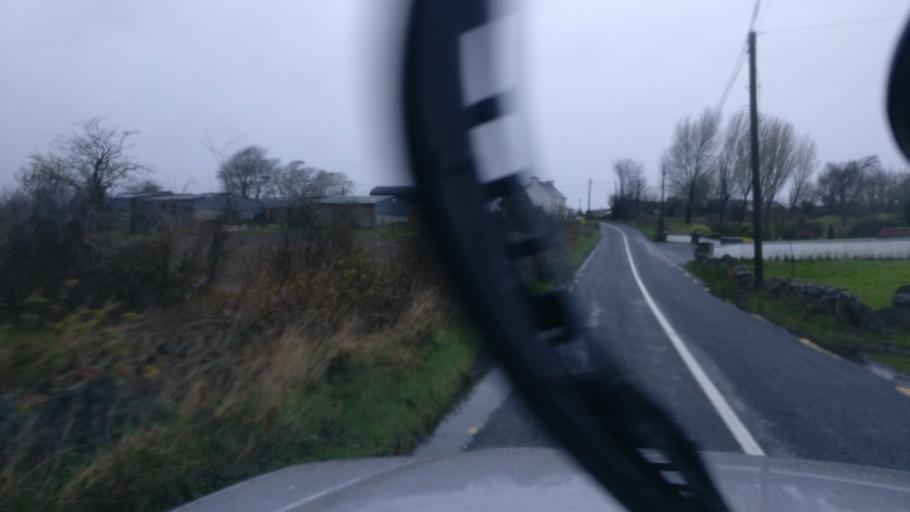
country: IE
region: Connaught
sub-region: County Galway
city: Loughrea
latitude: 53.1158
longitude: -8.4414
